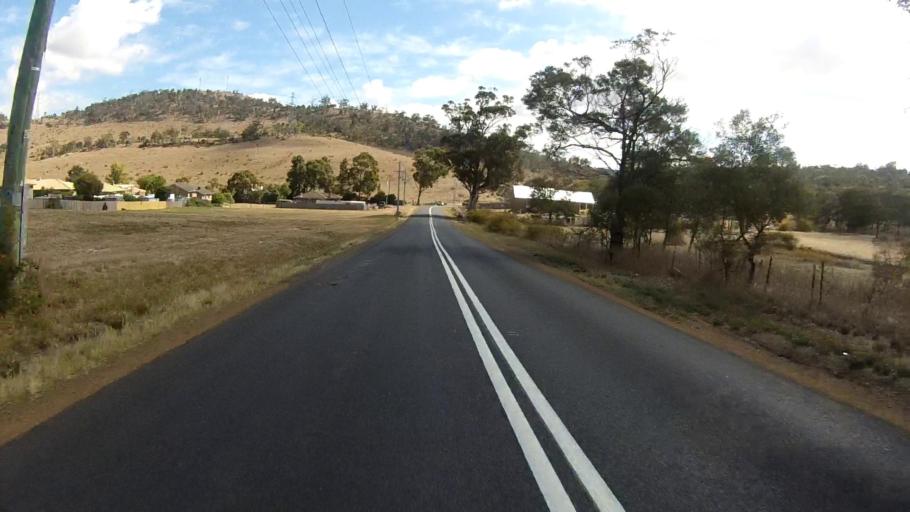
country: AU
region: Tasmania
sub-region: Brighton
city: Old Beach
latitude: -42.7479
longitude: 147.2807
